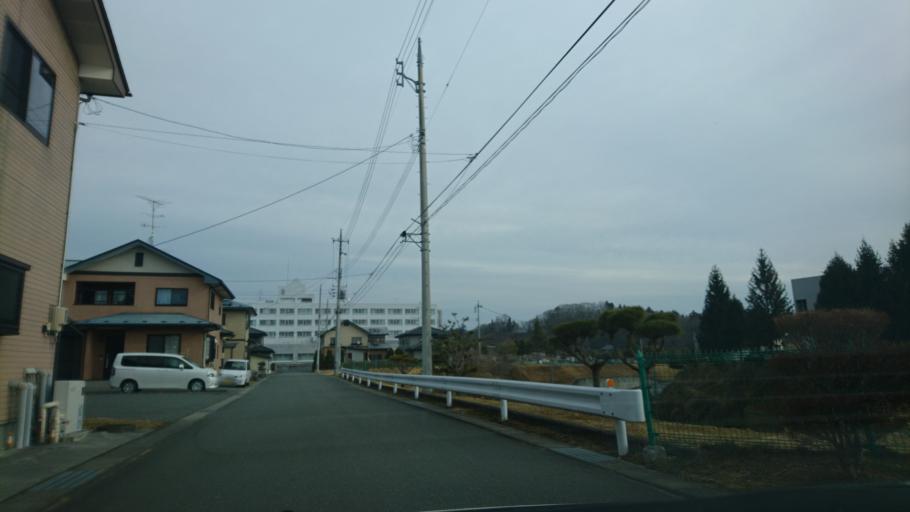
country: JP
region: Iwate
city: Ichinoseki
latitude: 38.9264
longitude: 141.3425
